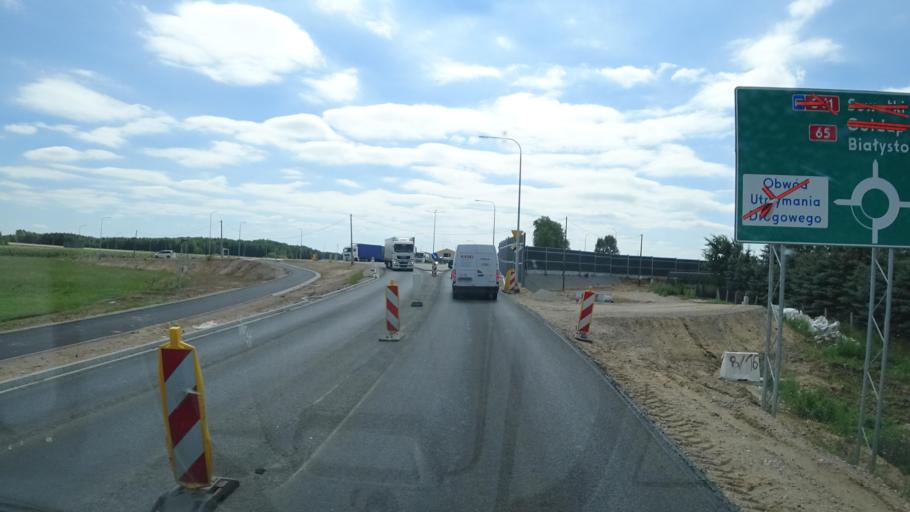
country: PL
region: Warmian-Masurian Voivodeship
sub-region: Powiat elcki
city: Elk
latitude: 53.7600
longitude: 22.3382
